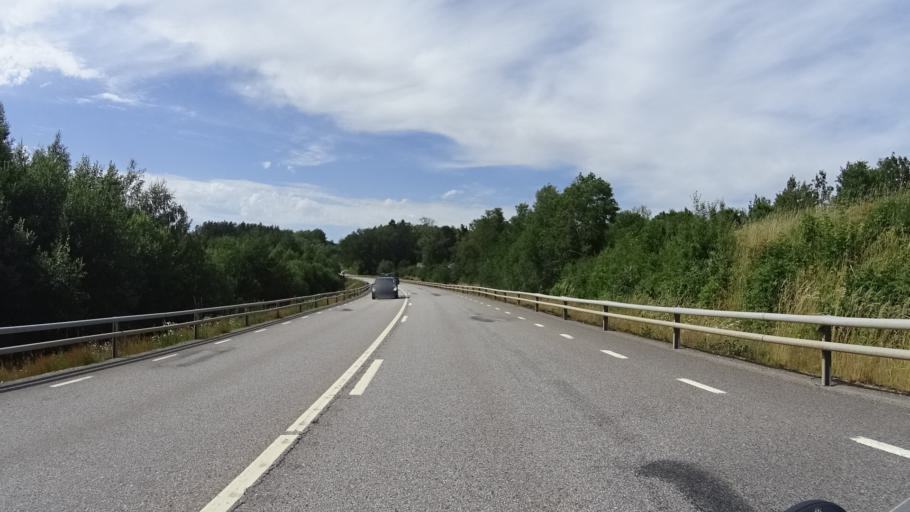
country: SE
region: Kalmar
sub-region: Vasterviks Kommun
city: Overum
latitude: 57.9805
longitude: 16.3275
